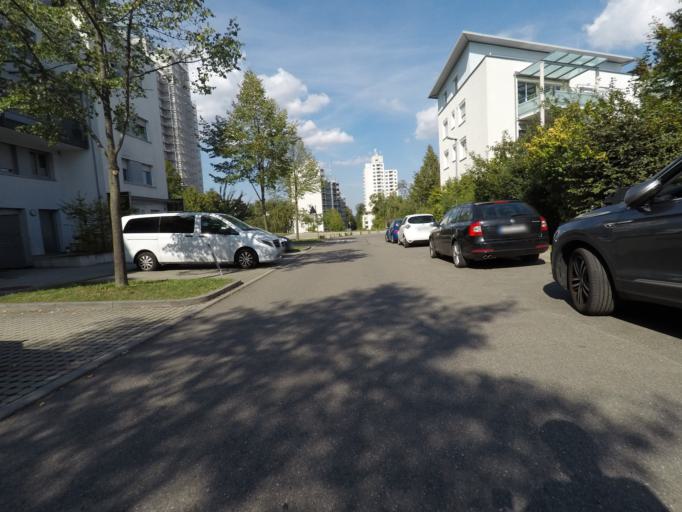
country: DE
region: Baden-Wuerttemberg
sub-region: Regierungsbezirk Stuttgart
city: Gerlingen
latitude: 48.7361
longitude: 9.0895
